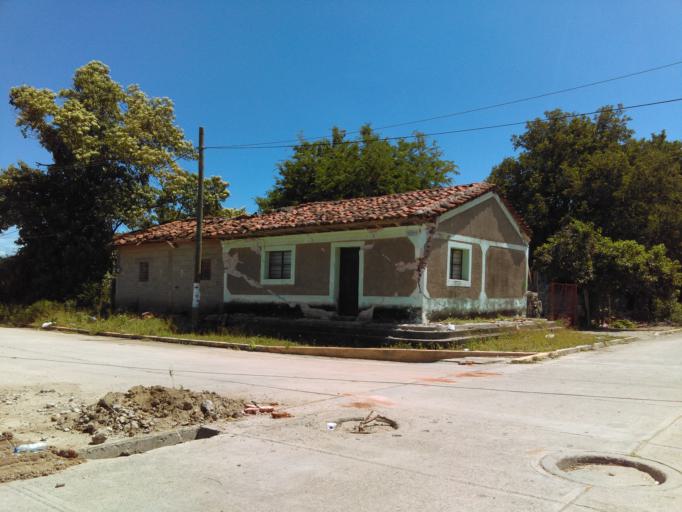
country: MX
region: Oaxaca
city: Asuncion Ixtaltepec
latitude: 16.5057
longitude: -95.0601
